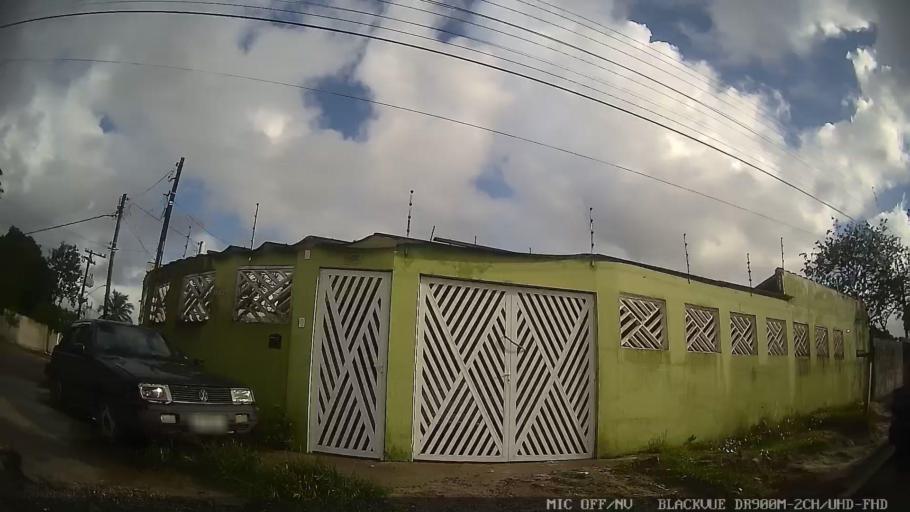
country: BR
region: Sao Paulo
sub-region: Itanhaem
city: Itanhaem
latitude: -24.1775
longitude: -46.8521
